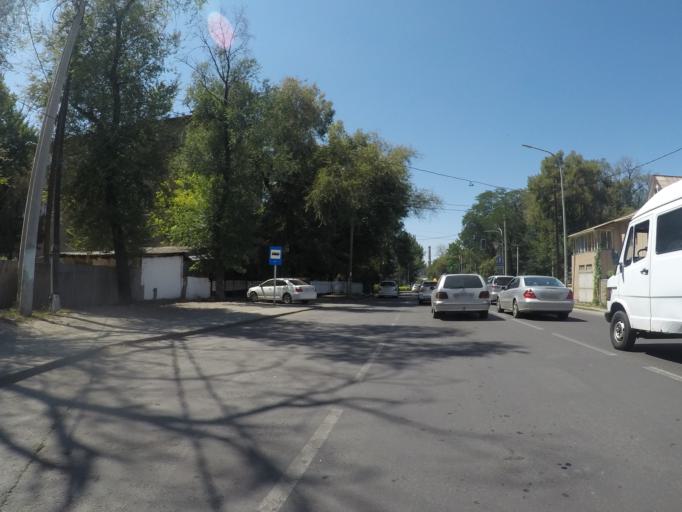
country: KG
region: Chuy
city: Bishkek
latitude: 42.8683
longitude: 74.5761
